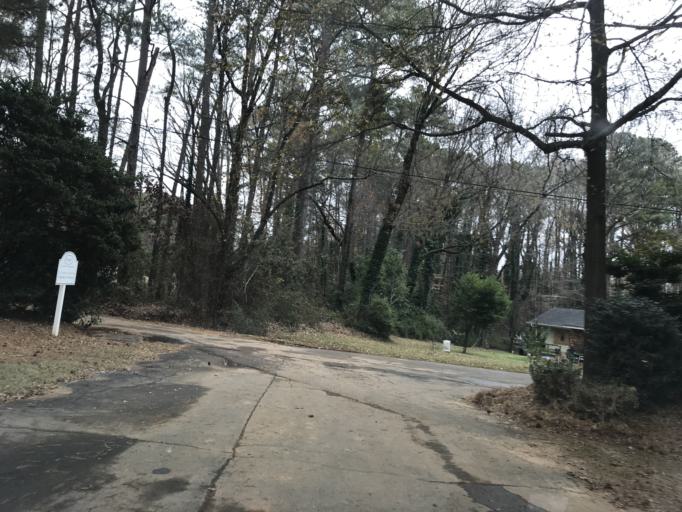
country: US
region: Georgia
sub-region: DeKalb County
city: Clarkston
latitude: 33.8336
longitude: -84.2481
